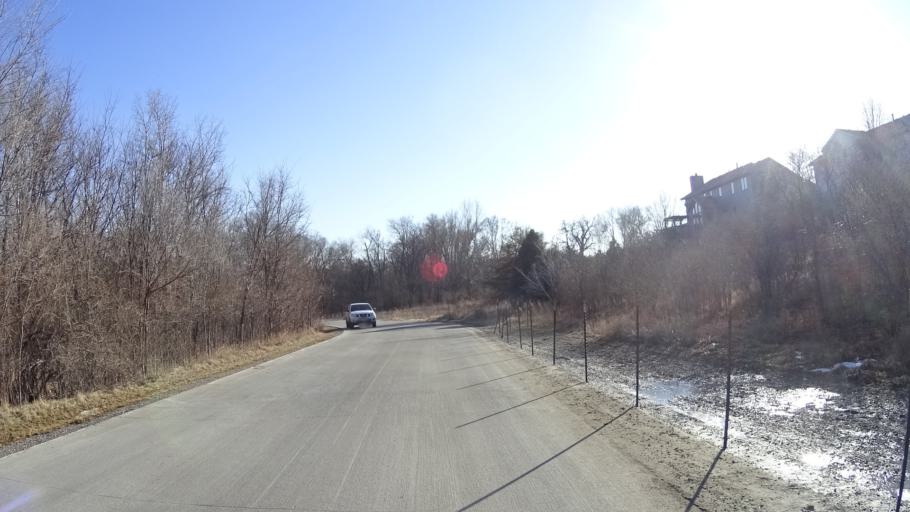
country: US
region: Nebraska
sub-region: Douglas County
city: Bennington
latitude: 41.3089
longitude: -96.1314
